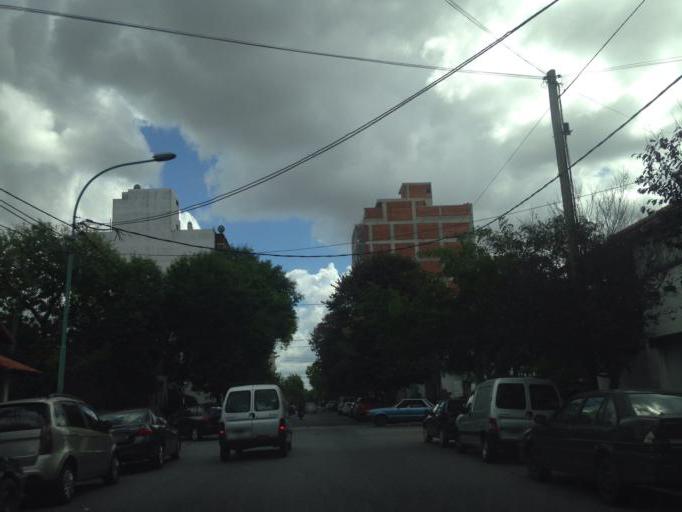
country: AR
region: Buenos Aires
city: Mar del Plata
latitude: -38.0082
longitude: -57.5520
